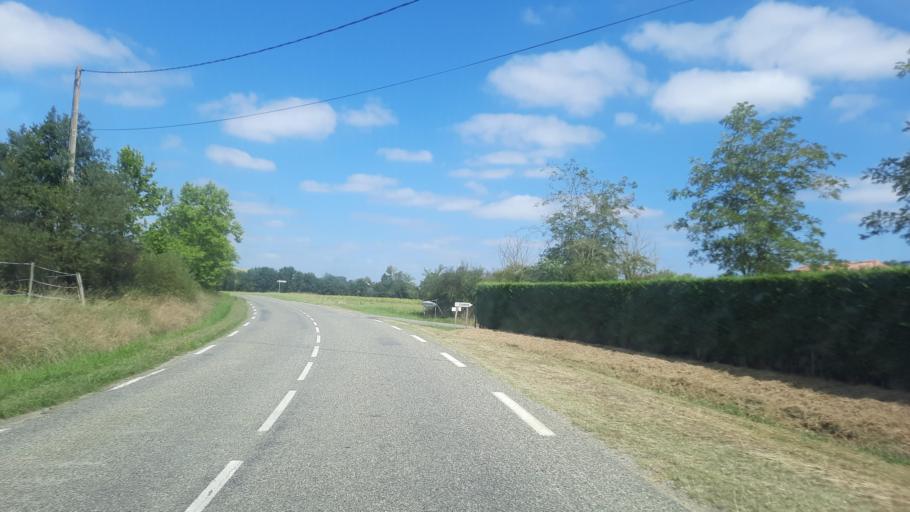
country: FR
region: Midi-Pyrenees
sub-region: Departement du Gers
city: Lombez
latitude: 43.4288
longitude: 0.8368
